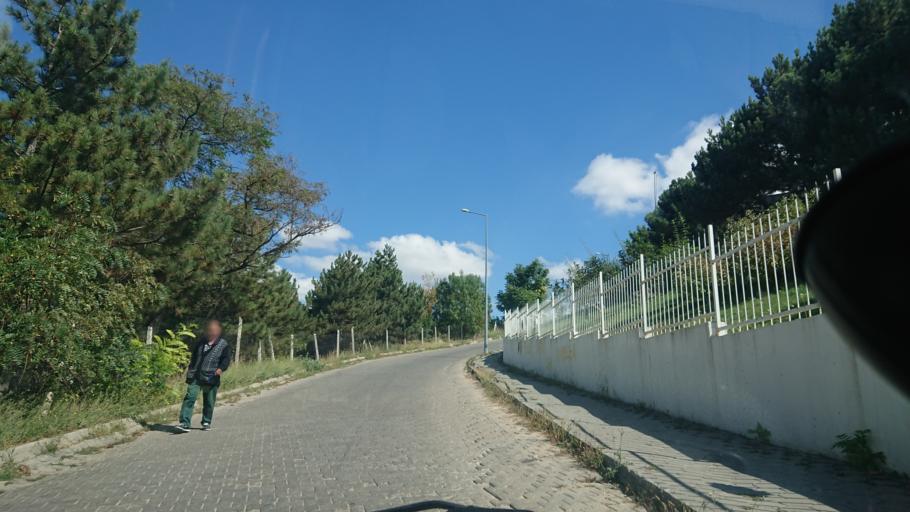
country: TR
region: Eskisehir
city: Eskisehir
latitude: 39.7588
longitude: 30.5325
